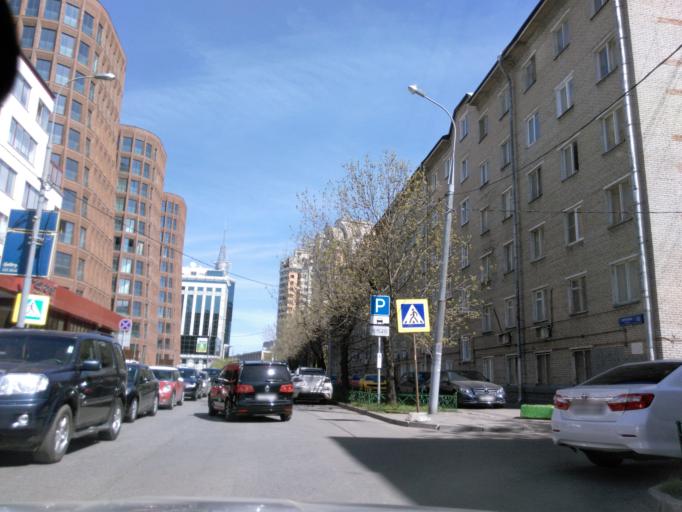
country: RU
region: Moscow
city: Luzhniki
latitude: 55.7244
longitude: 37.5733
